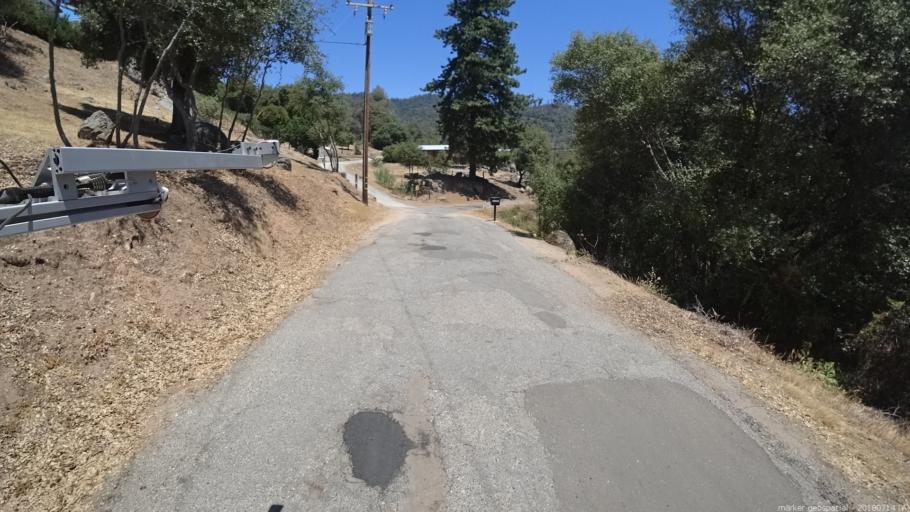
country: US
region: California
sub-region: Madera County
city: Ahwahnee
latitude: 37.4162
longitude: -119.7161
